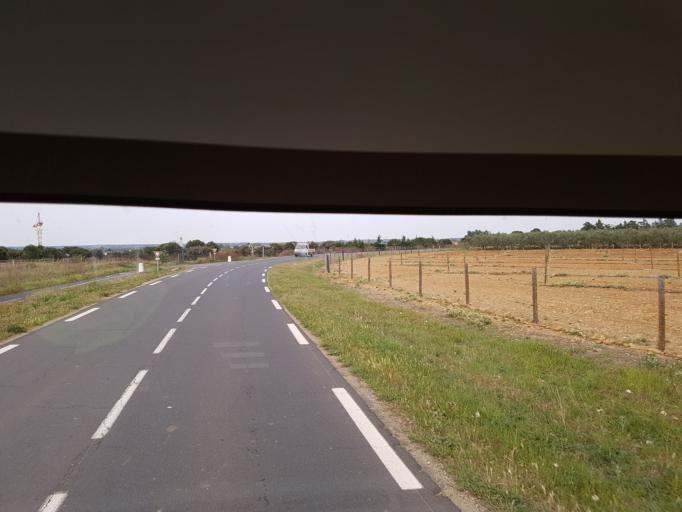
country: FR
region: Languedoc-Roussillon
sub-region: Departement de l'Herault
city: Serignan
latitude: 43.2744
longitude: 3.2638
